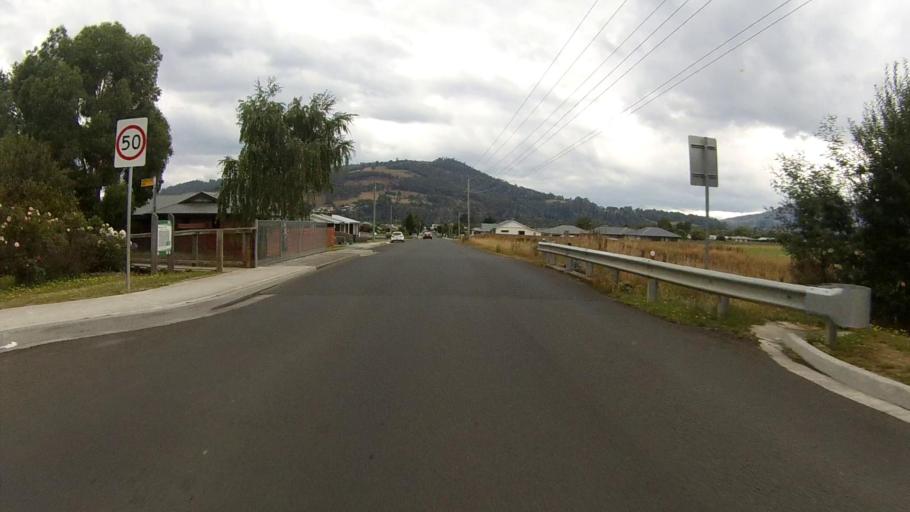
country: AU
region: Tasmania
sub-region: Huon Valley
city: Huonville
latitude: -43.0288
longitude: 147.0586
